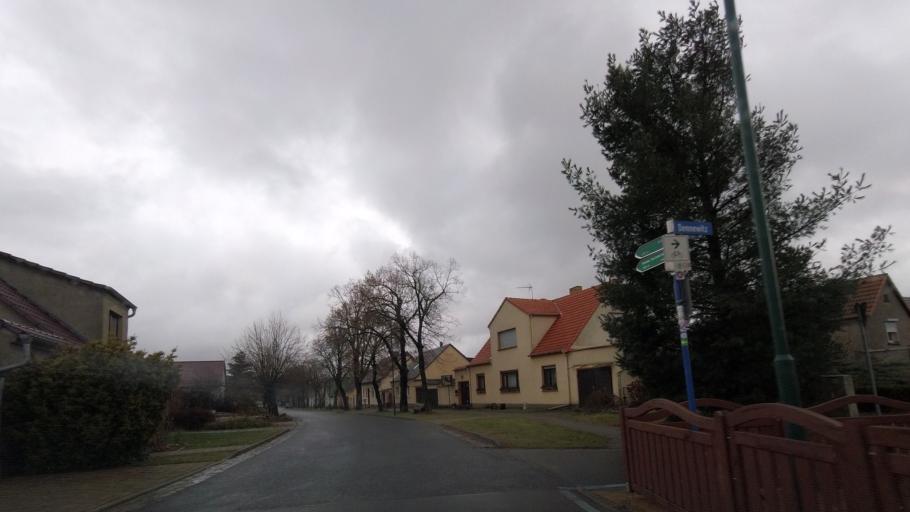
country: DE
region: Brandenburg
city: Niedergorsdorf
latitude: 51.9706
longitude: 13.0065
